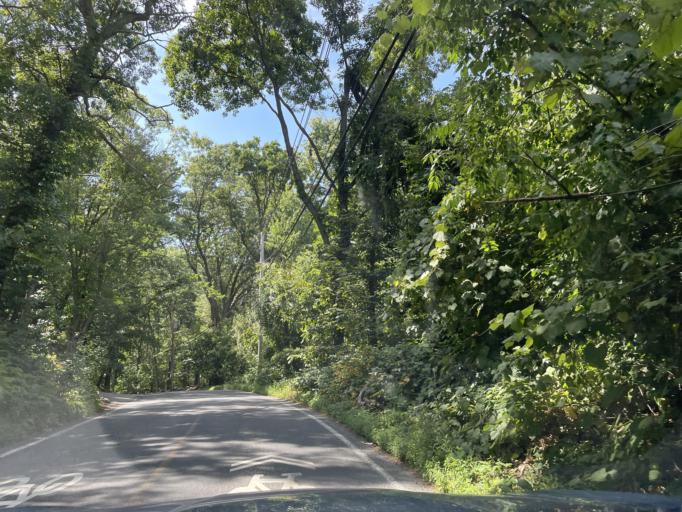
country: US
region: Massachusetts
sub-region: Middlesex County
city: Sherborn
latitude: 42.2378
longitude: -71.4068
